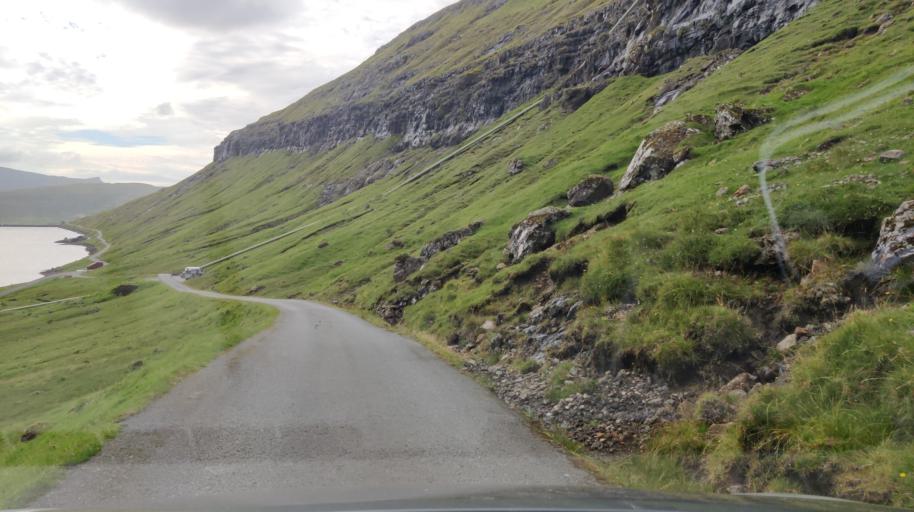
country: FO
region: Streymoy
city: Vestmanna
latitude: 62.1554
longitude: -7.1035
